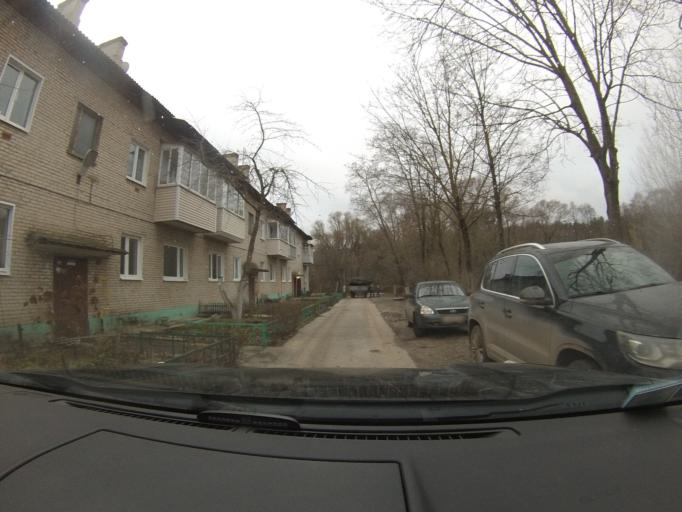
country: RU
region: Moskovskaya
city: Peski
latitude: 55.2613
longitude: 38.7638
